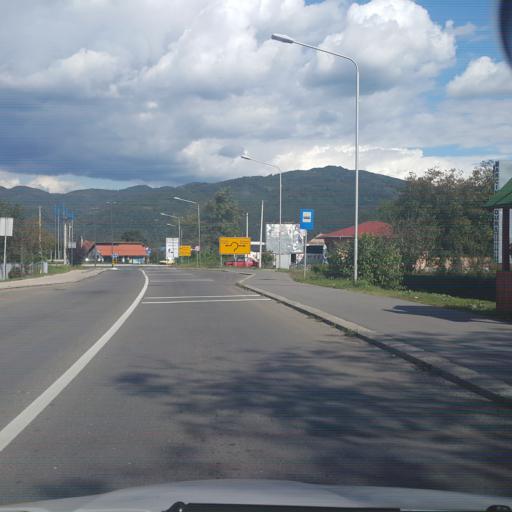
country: RS
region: Central Serbia
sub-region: Raski Okrug
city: Vrnjacka Banja
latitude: 43.6389
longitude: 20.9197
